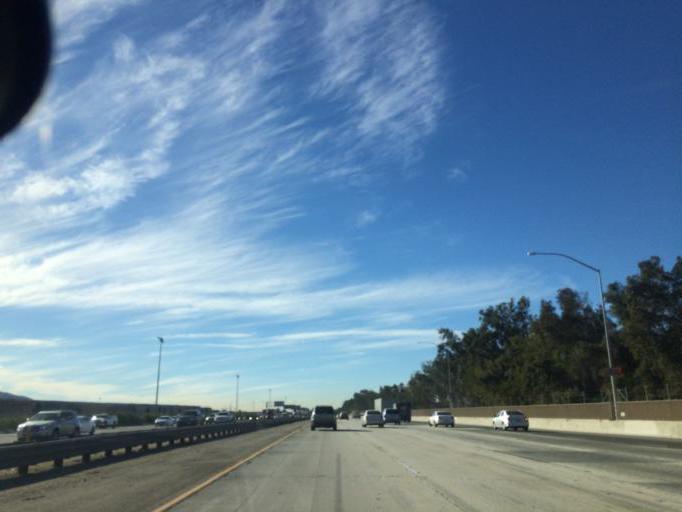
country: US
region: California
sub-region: San Bernardino County
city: Bloomington
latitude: 34.0686
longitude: -117.3752
